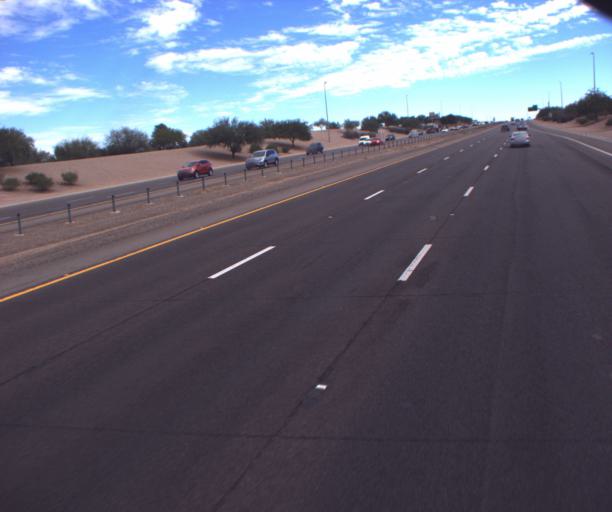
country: US
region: Arizona
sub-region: Maricopa County
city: Chandler
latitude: 33.2829
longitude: -111.7819
